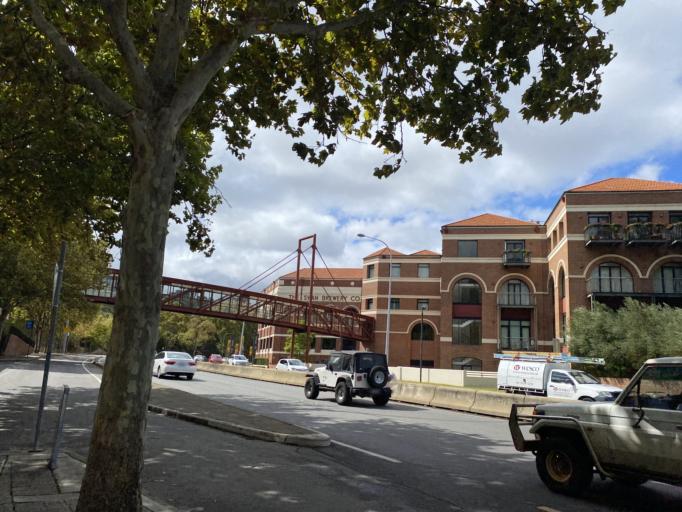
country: AU
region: Western Australia
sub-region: City of Perth
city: West Perth
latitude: -31.9657
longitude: 115.8397
